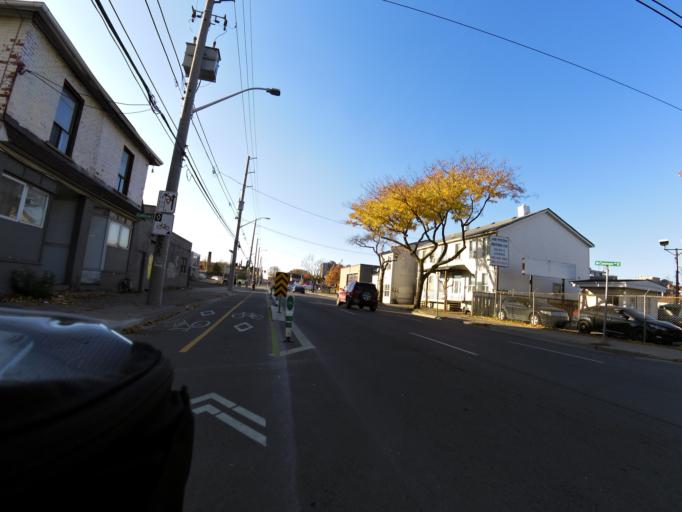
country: CA
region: Ontario
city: Hamilton
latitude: 43.2585
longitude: -79.8584
